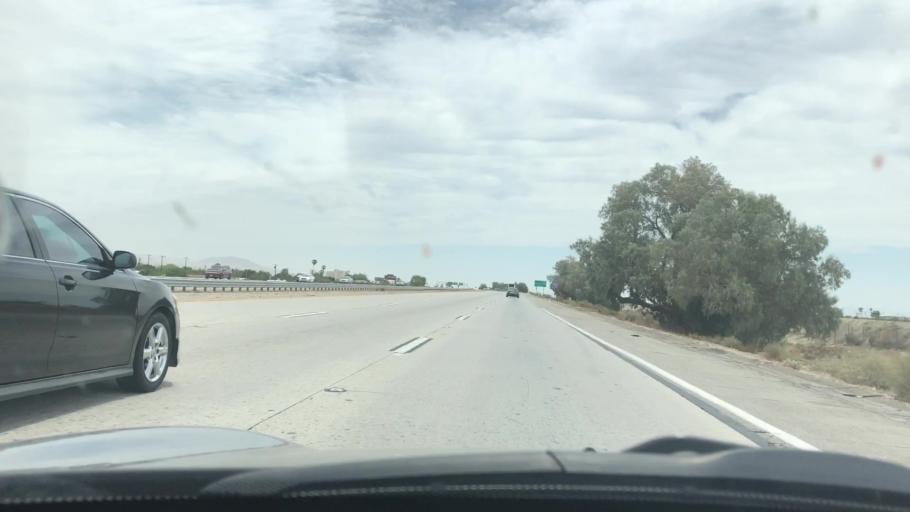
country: US
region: California
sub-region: Riverside County
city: Indio
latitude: 33.7344
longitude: -116.2111
